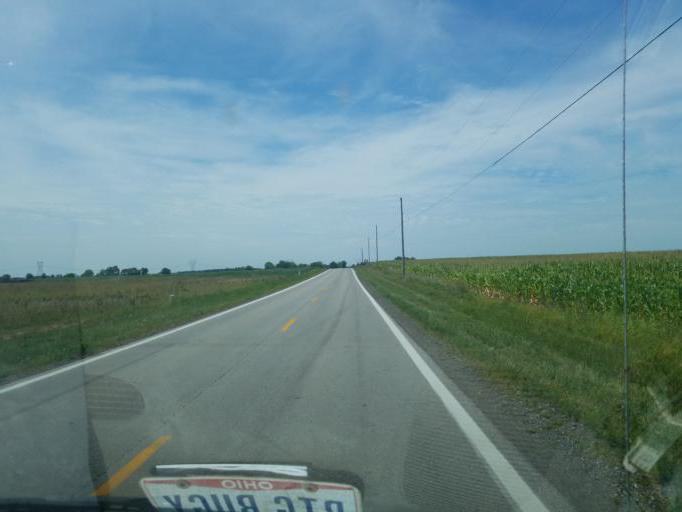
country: US
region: Ohio
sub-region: Madison County
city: West Jefferson
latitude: 39.8690
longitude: -83.2824
